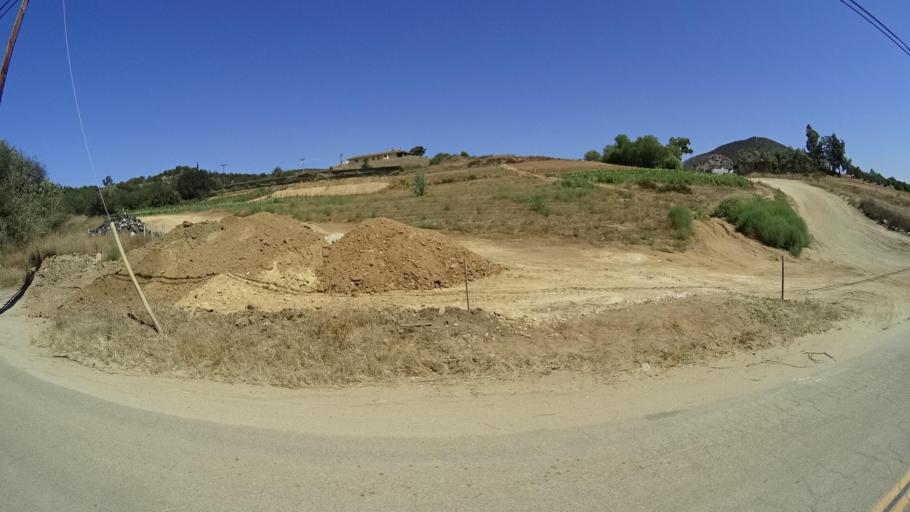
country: US
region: California
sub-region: San Diego County
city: Hidden Meadows
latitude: 33.3074
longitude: -117.0833
